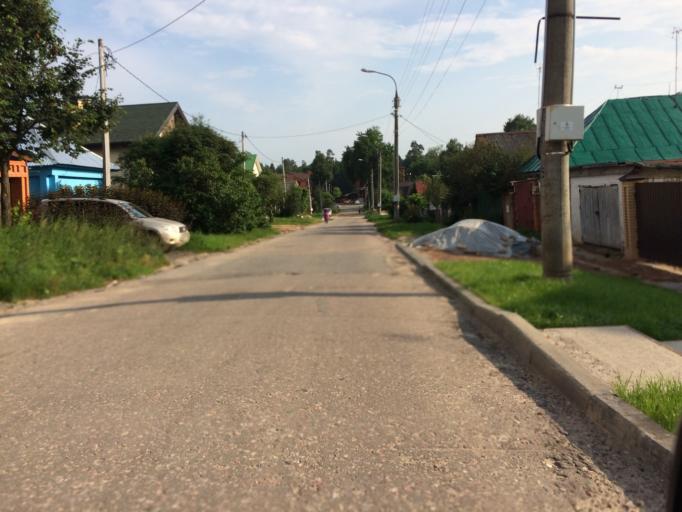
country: RU
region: Mariy-El
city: Yoshkar-Ola
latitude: 56.6190
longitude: 47.9448
